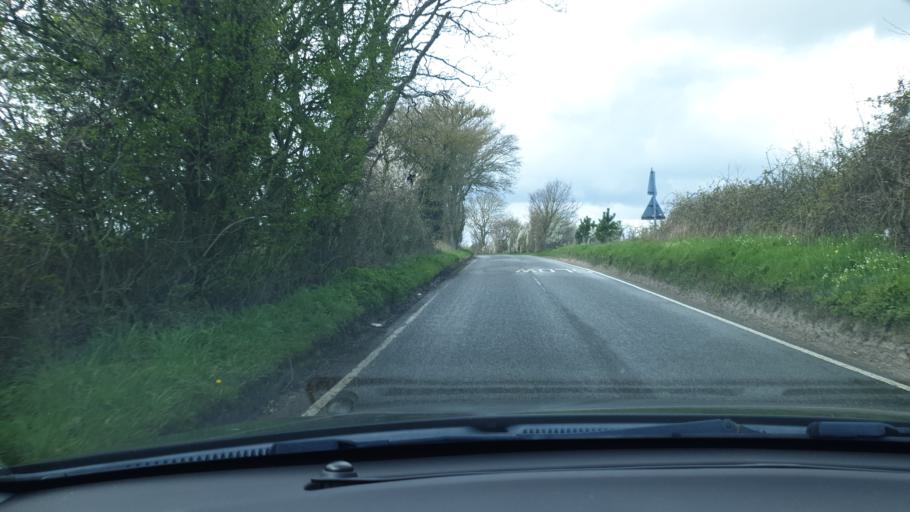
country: GB
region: England
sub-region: Essex
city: Little Clacton
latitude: 51.9045
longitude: 1.1790
